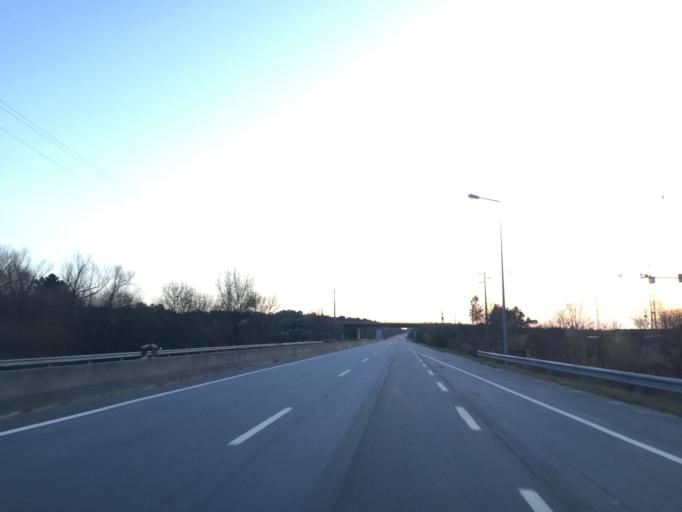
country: PT
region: Viseu
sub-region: Concelho de Carregal do Sal
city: Carregal do Sal
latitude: 40.4543
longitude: -7.9731
